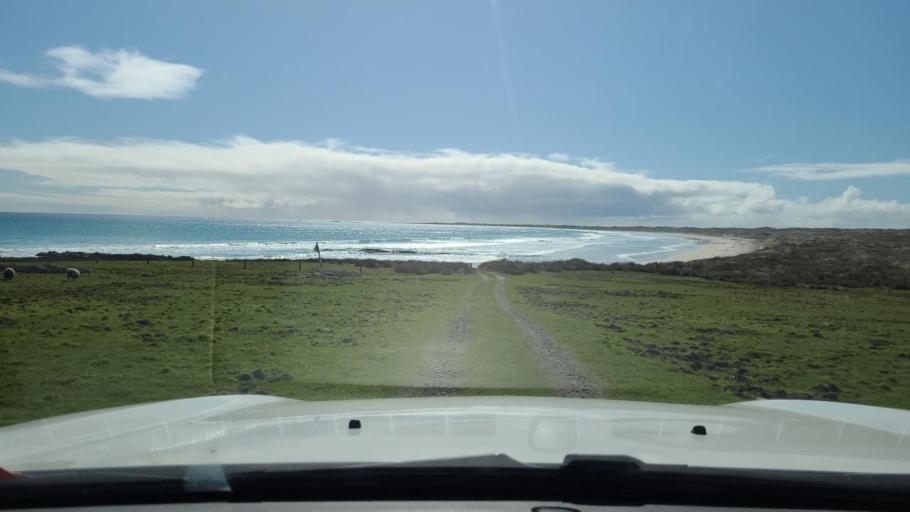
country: NZ
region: Chatham Islands
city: Waitangi
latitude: -43.7856
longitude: -176.8113
